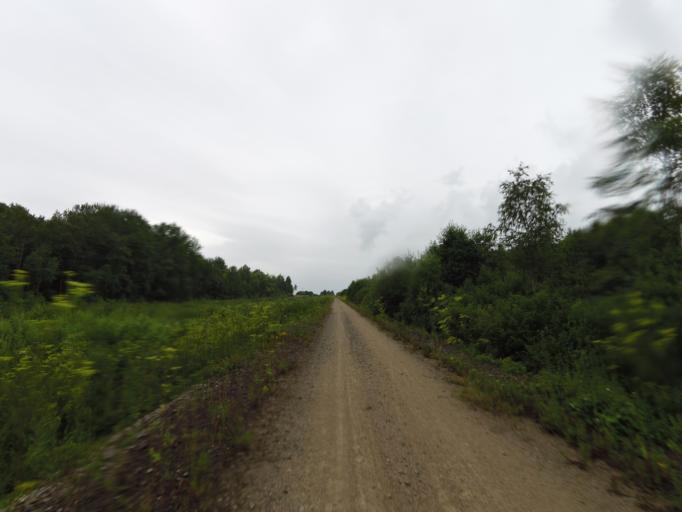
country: EE
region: Laeaene
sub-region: Ridala Parish
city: Uuemoisa
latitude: 58.9546
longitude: 23.8257
